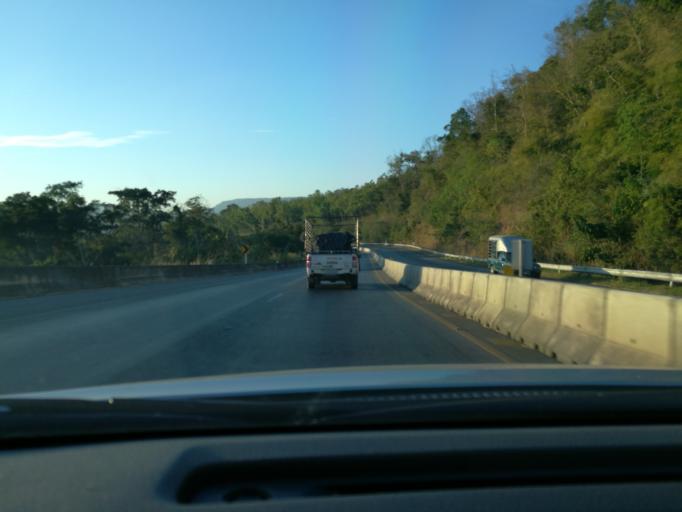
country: TH
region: Phitsanulok
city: Wang Thong
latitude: 16.8540
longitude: 100.5111
